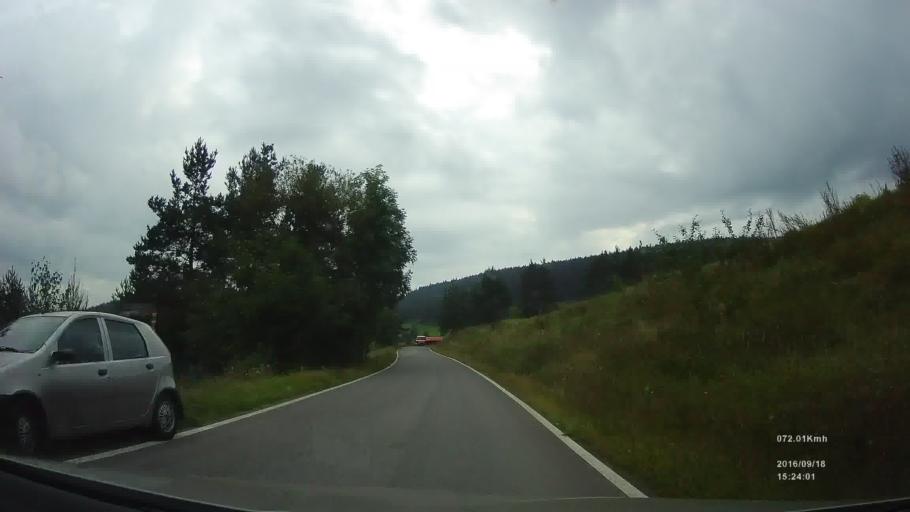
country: SK
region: Presovsky
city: Lubica
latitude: 49.0361
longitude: 20.4896
